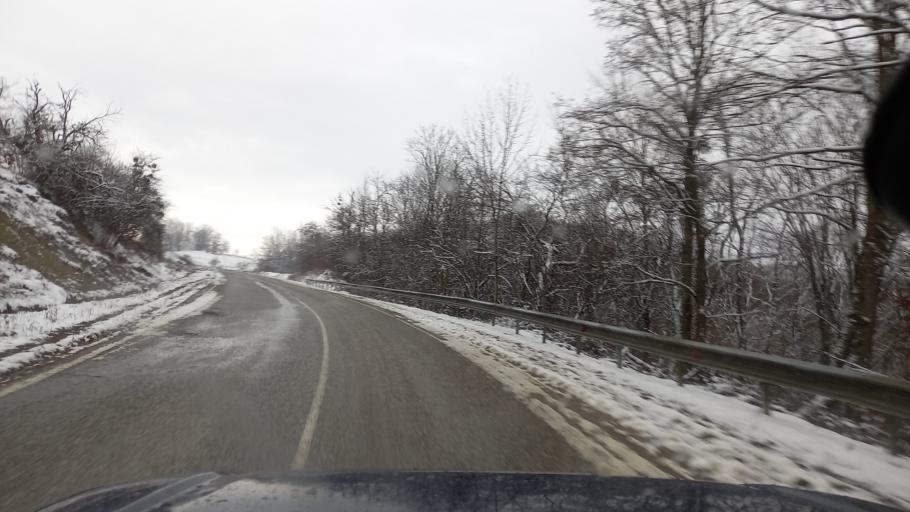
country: RU
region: Adygeya
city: Abadzekhskaya
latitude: 44.3485
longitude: 40.3292
